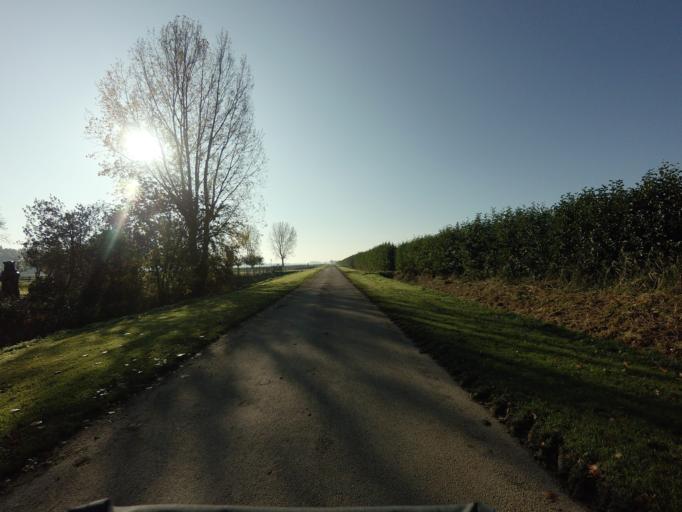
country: NL
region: North Brabant
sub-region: Gemeente Werkendam
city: Werkendam
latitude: 51.7964
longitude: 4.8839
